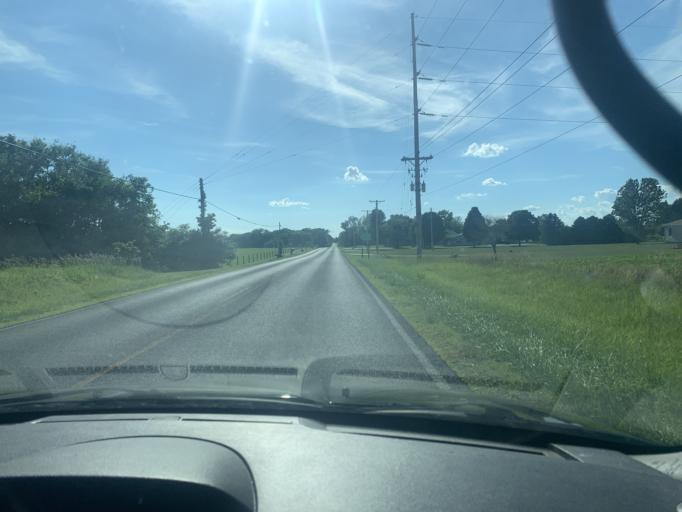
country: US
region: Ohio
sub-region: Logan County
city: Bellefontaine
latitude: 40.3480
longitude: -83.7835
